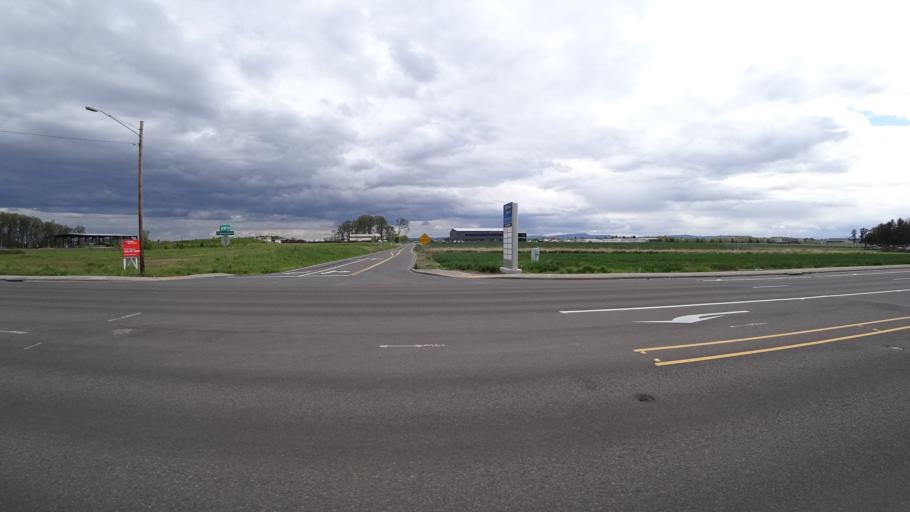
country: US
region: Oregon
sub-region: Washington County
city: Hillsboro
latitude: 45.5512
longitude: -122.9483
